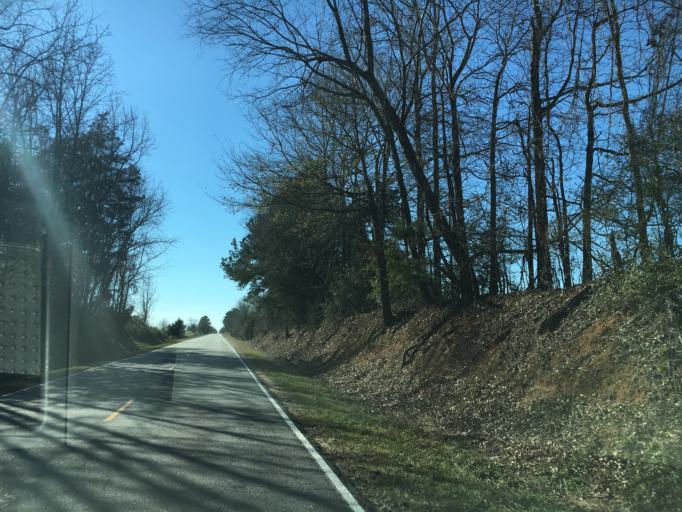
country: US
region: South Carolina
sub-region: Anderson County
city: Iva
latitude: 34.3642
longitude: -82.7168
